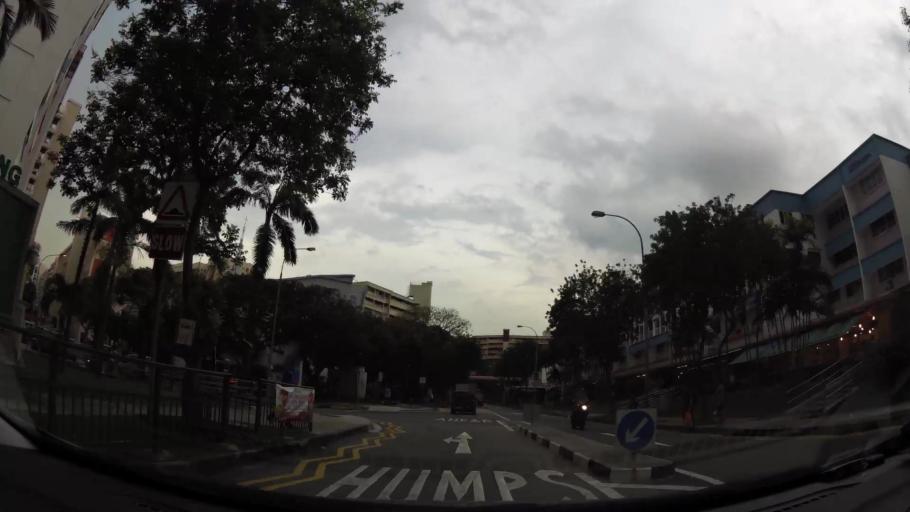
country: MY
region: Johor
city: Kampung Pasir Gudang Baru
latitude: 1.4374
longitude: 103.8372
